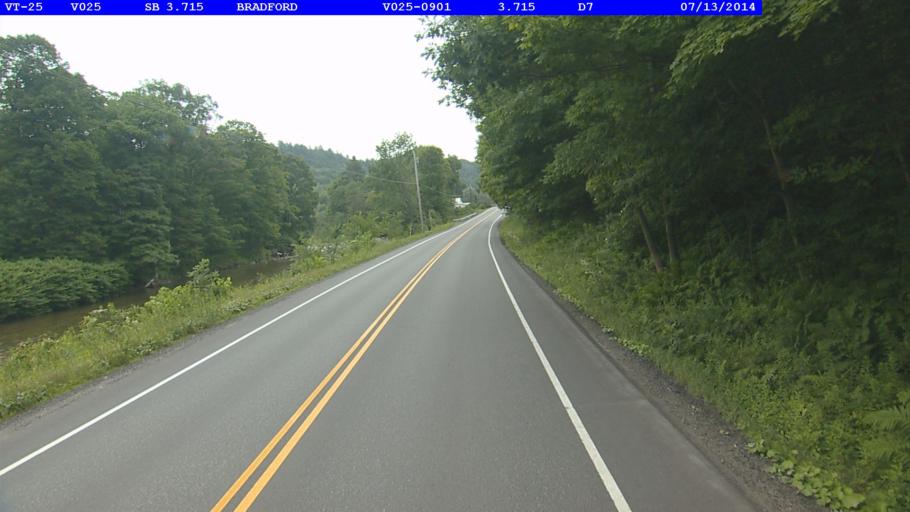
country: US
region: New Hampshire
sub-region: Grafton County
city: Orford
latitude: 44.0075
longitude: -72.1659
